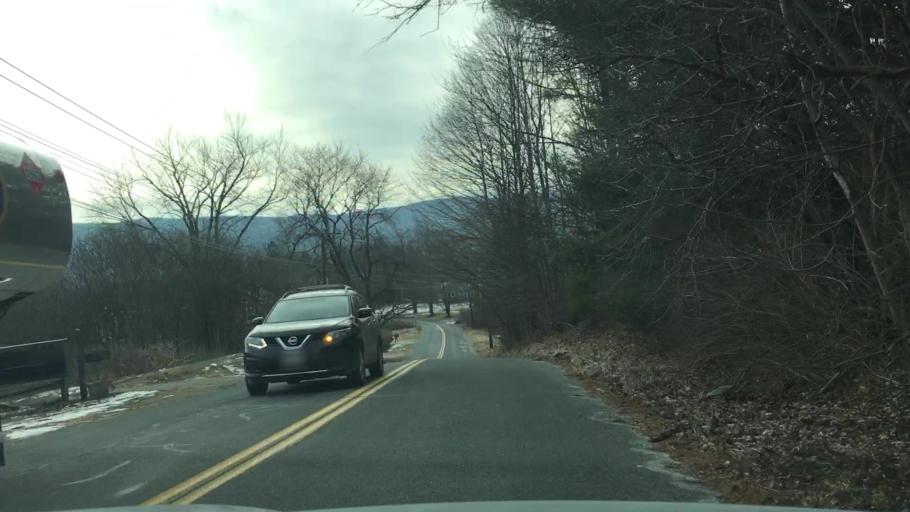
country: US
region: Massachusetts
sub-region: Berkshire County
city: Lee
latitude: 42.2880
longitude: -73.2453
